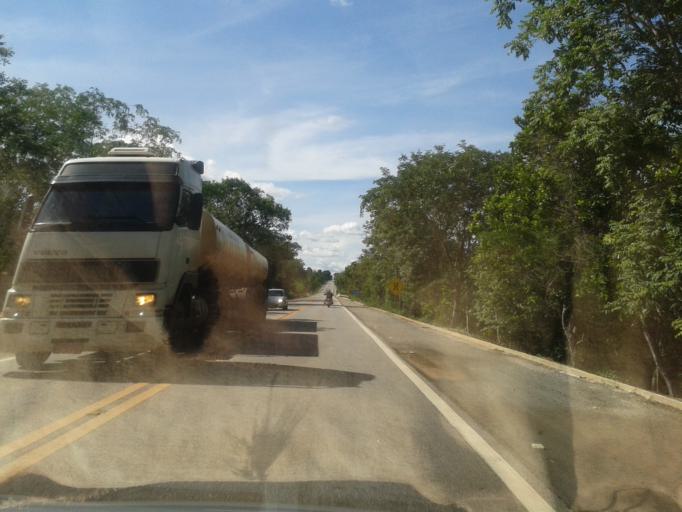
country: BR
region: Goias
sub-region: Itapirapua
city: Itapirapua
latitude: -15.2897
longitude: -50.4687
